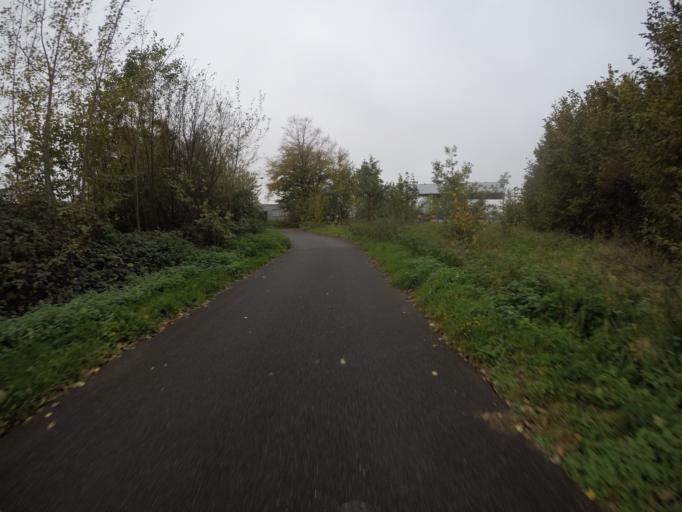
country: DE
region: North Rhine-Westphalia
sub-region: Regierungsbezirk Dusseldorf
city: Bocholt
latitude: 51.8168
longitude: 6.5779
